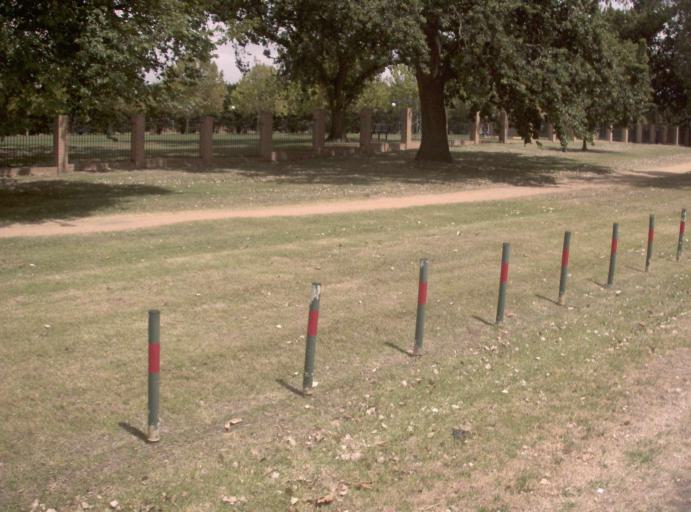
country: AU
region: Victoria
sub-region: Casey
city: Berwick
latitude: -38.0420
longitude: 145.3640
